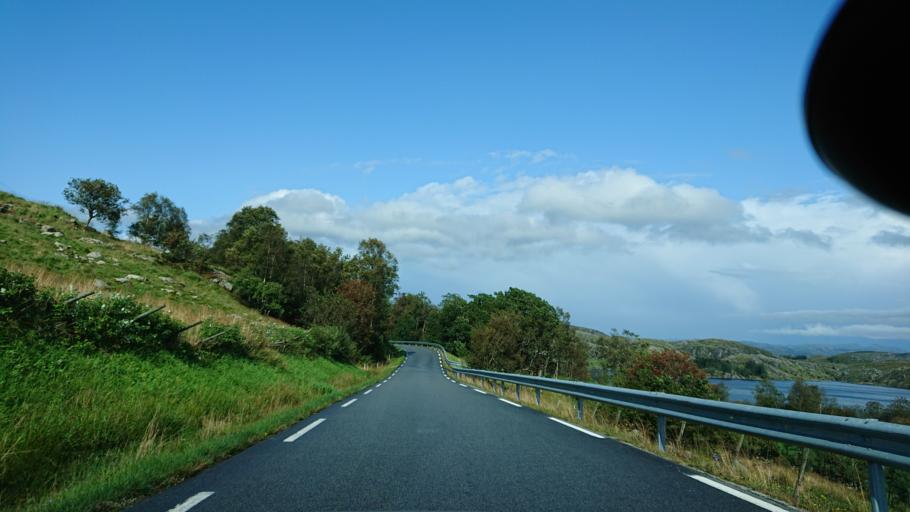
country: NO
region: Rogaland
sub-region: Gjesdal
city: Algard
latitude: 58.6911
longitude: 5.8795
